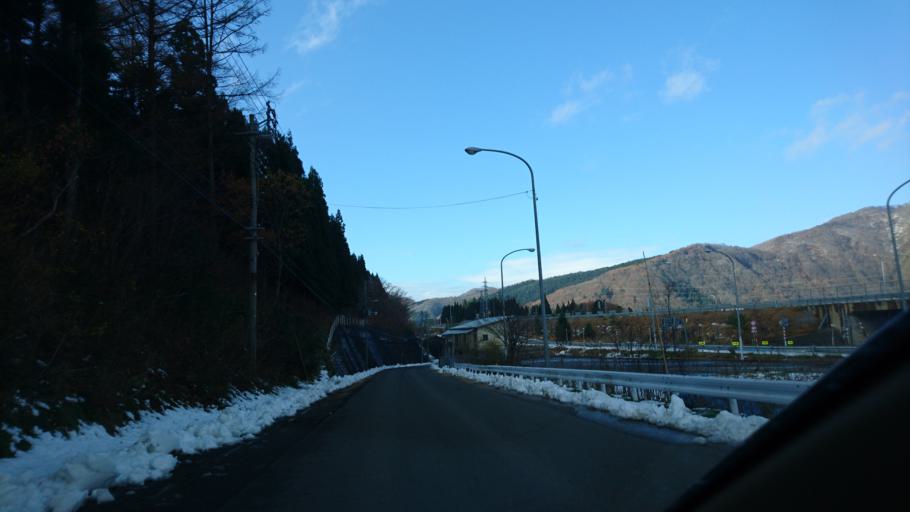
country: JP
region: Iwate
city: Kitakami
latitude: 39.2910
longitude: 140.8405
